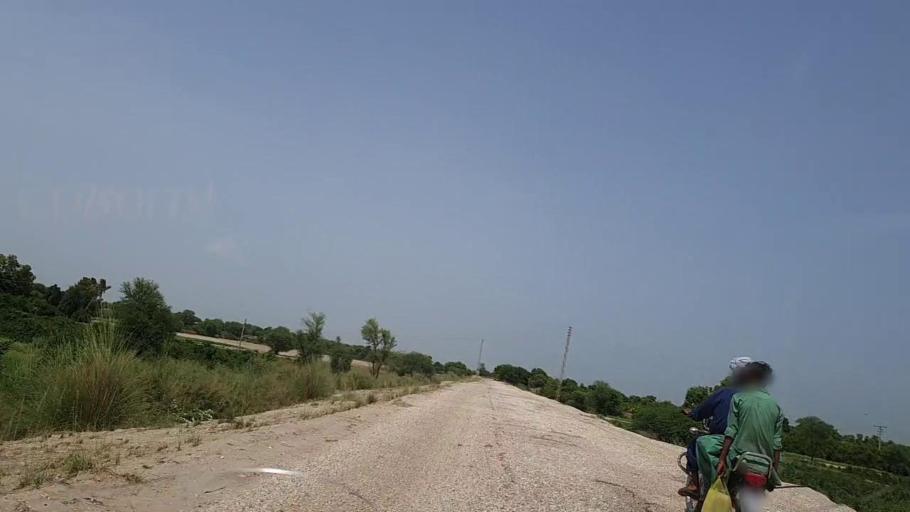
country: PK
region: Sindh
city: Tharu Shah
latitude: 27.0414
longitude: 68.1120
